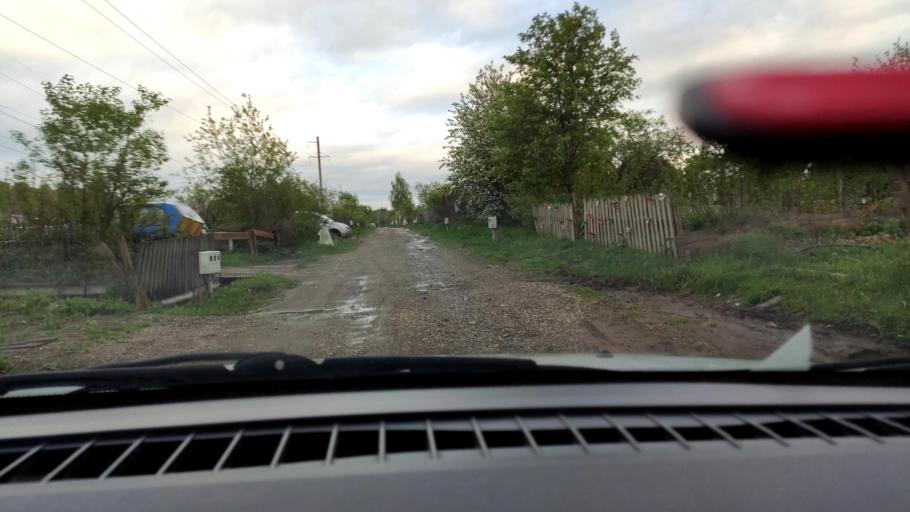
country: RU
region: Perm
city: Polazna
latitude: 58.1294
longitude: 56.4148
